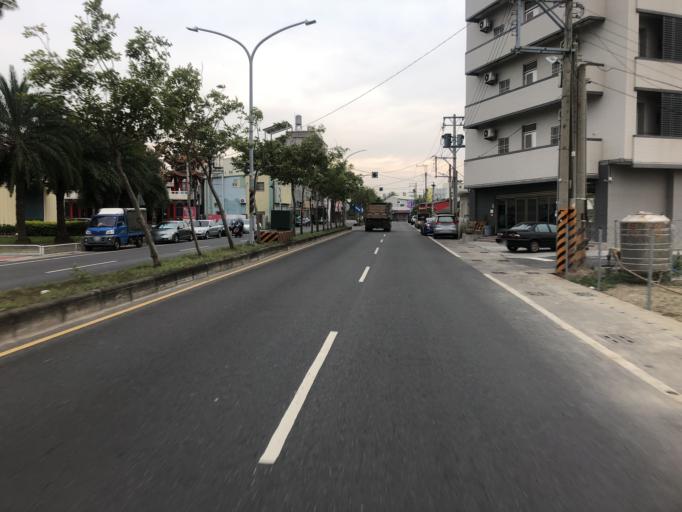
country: TW
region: Taiwan
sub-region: Tainan
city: Tainan
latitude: 23.1349
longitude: 120.2852
